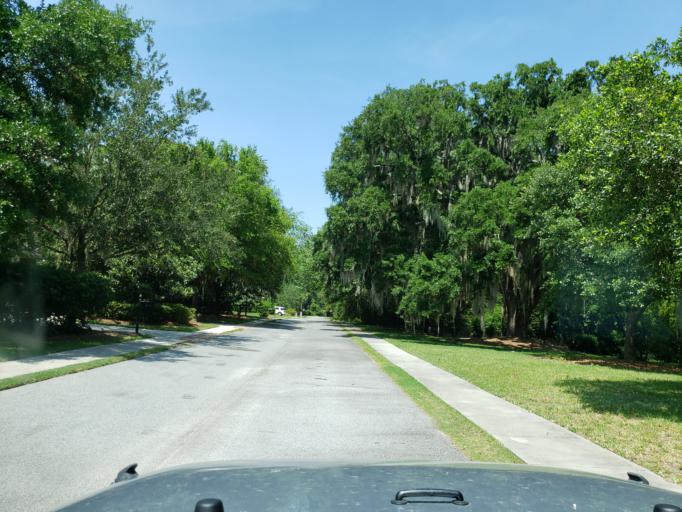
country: US
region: Georgia
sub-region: Chatham County
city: Whitemarsh Island
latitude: 32.0195
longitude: -81.0147
